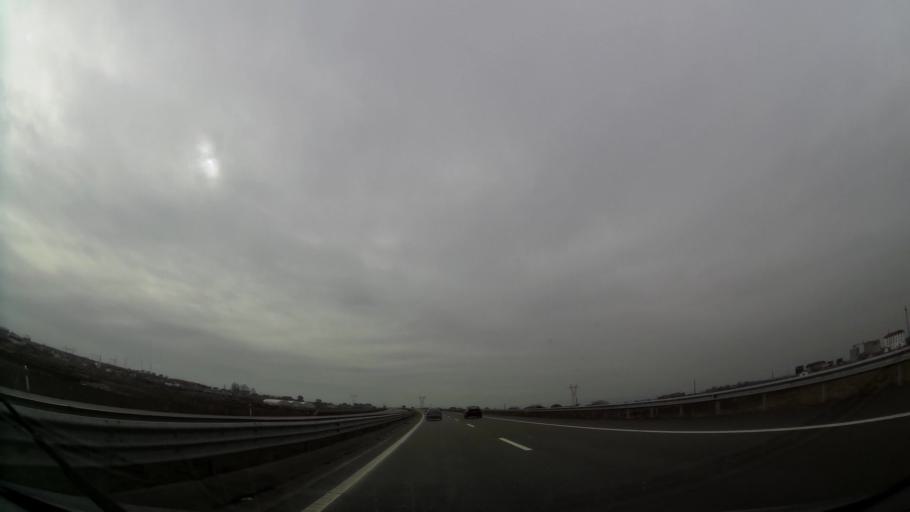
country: XK
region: Pristina
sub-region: Lipjan
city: Lipljan
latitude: 42.4796
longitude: 21.1851
